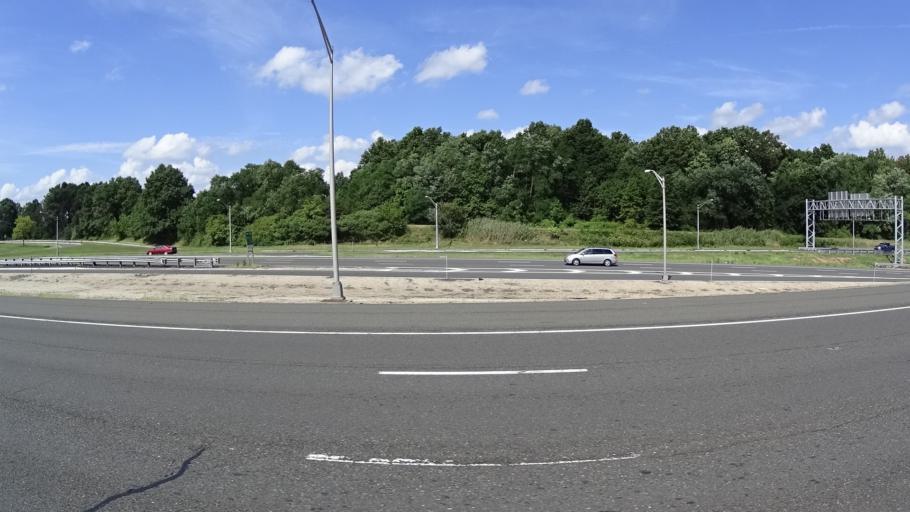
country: US
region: New Jersey
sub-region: Middlesex County
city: Fords
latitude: 40.5278
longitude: -74.2988
